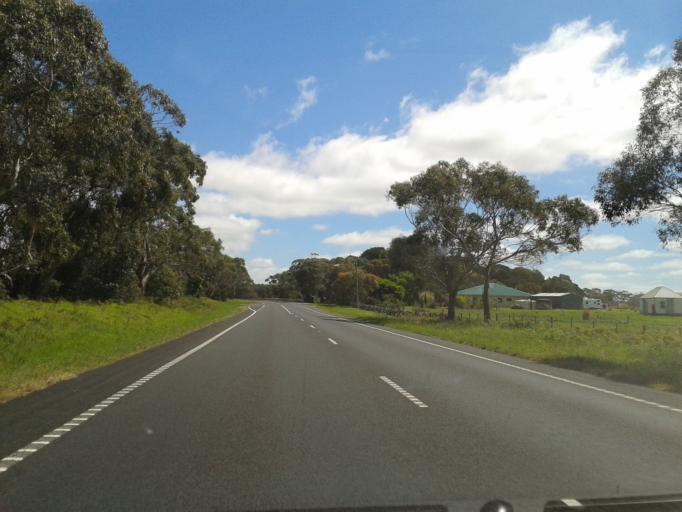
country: AU
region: Victoria
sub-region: Glenelg
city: Portland
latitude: -38.2333
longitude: 141.8522
